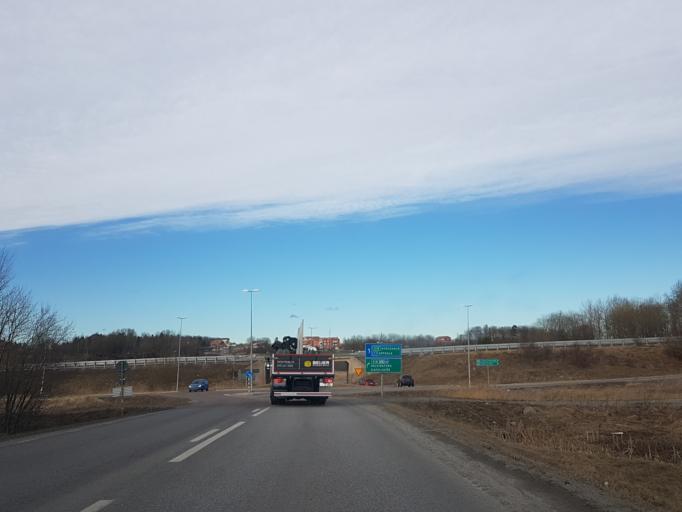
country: SE
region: Stockholm
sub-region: Norrtalje Kommun
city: Norrtalje
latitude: 59.7406
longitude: 18.6887
